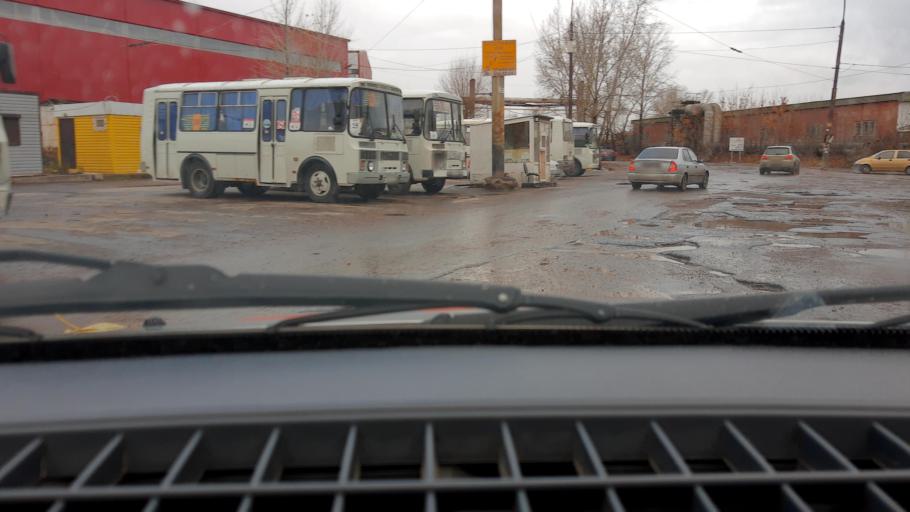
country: RU
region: Bashkortostan
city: Ufa
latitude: 54.8327
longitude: 56.1177
